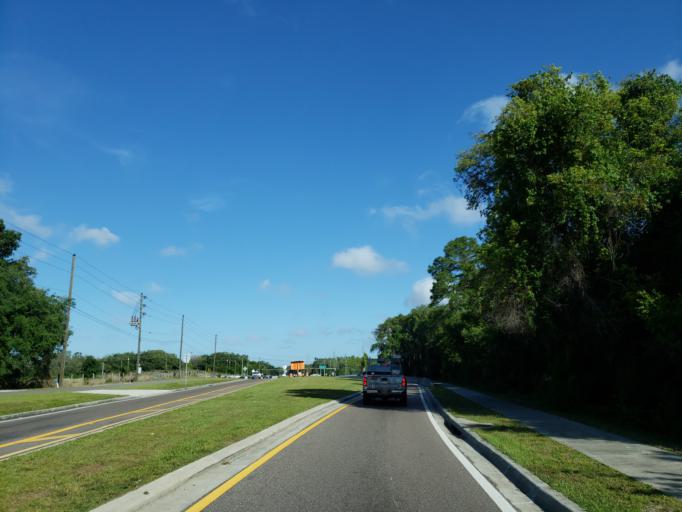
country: US
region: Florida
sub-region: Pasco County
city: Trinity
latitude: 28.1474
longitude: -82.6924
